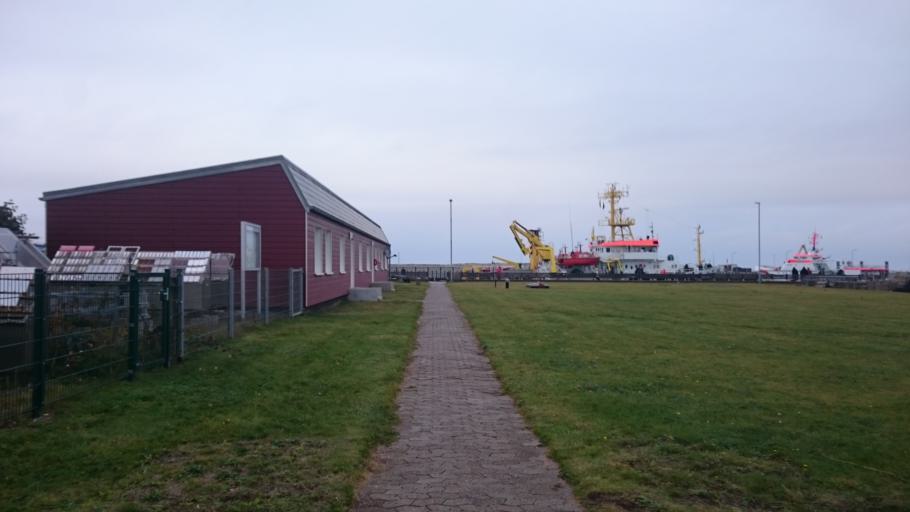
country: DE
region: Schleswig-Holstein
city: Helgoland
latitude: 54.1751
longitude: 7.8925
